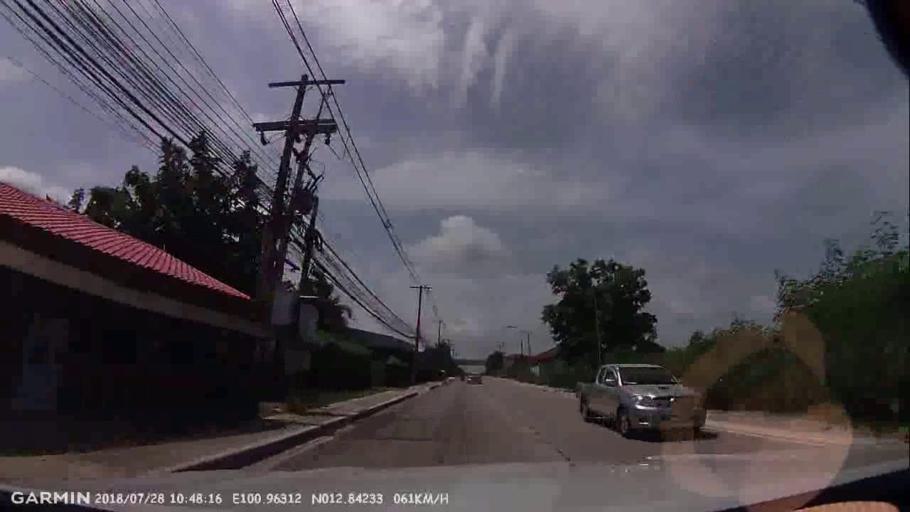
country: TH
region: Chon Buri
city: Phatthaya
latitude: 12.8422
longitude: 100.9632
